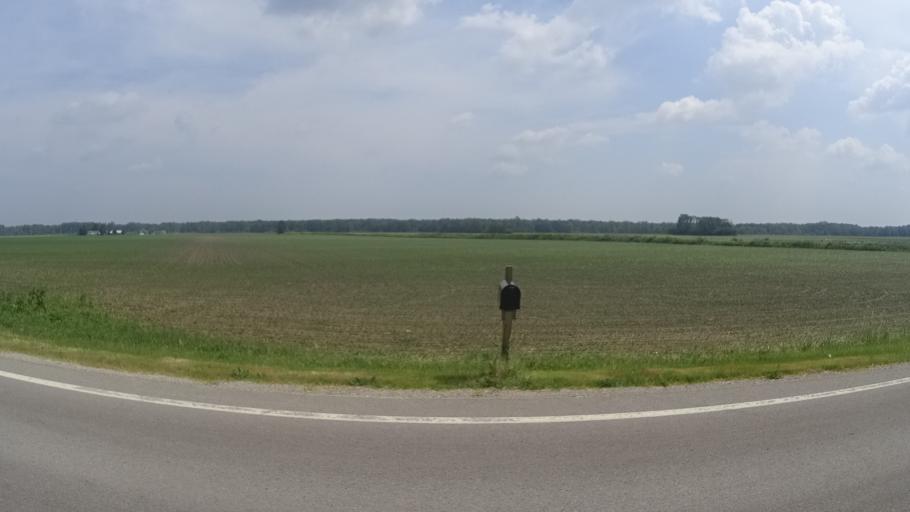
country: US
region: Ohio
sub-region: Erie County
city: Milan
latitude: 41.3478
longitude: -82.6918
